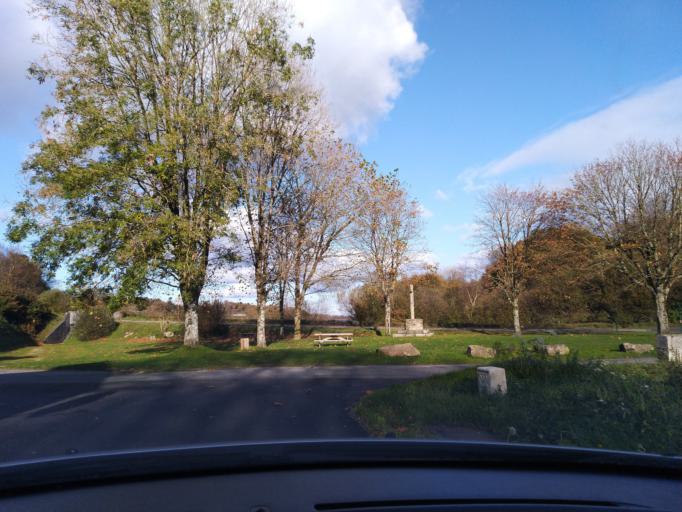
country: FR
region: Brittany
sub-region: Departement du Finistere
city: Guerlesquin
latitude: 48.5136
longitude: -3.5758
